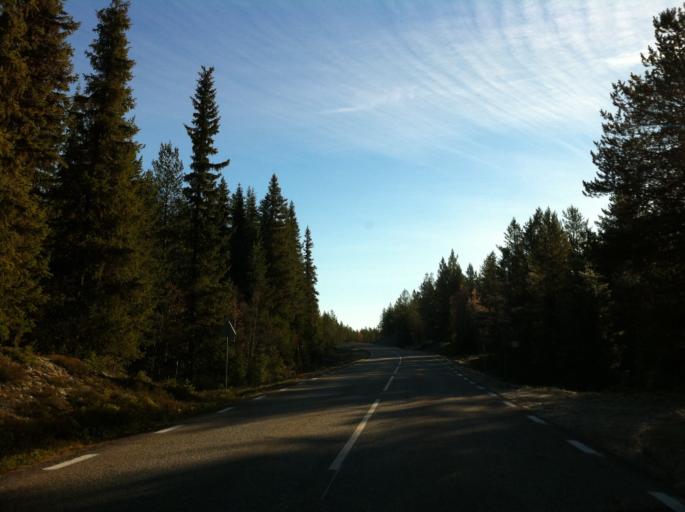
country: NO
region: Hedmark
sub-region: Engerdal
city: Engerdal
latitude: 61.9910
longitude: 12.4624
